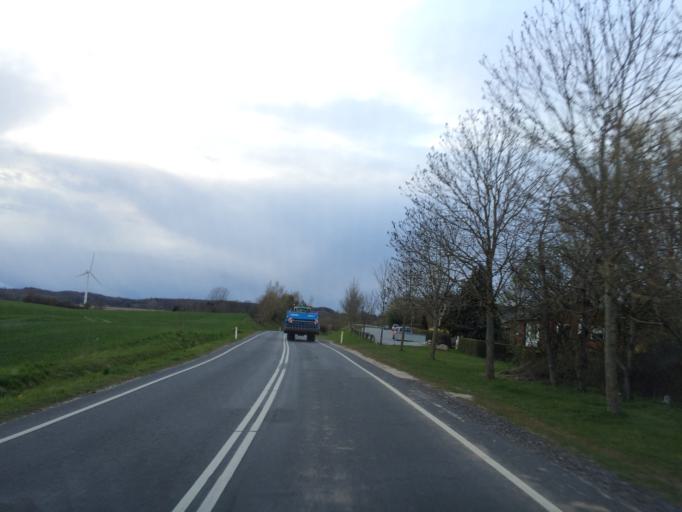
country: DK
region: South Denmark
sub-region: Odense Kommune
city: Bellinge
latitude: 55.3596
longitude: 10.2754
